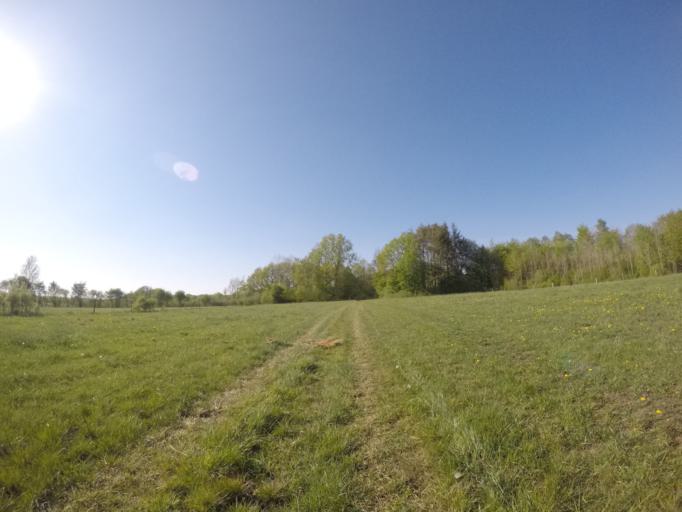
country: BE
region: Wallonia
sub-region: Province du Luxembourg
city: Tintigny
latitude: 49.7209
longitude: 5.5256
